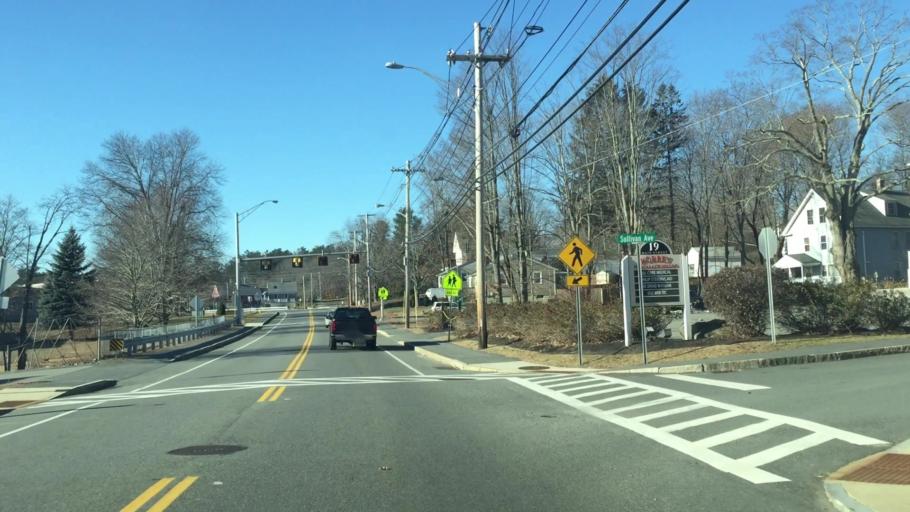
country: US
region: New Hampshire
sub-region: Rockingham County
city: Salem
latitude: 42.7824
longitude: -71.2360
